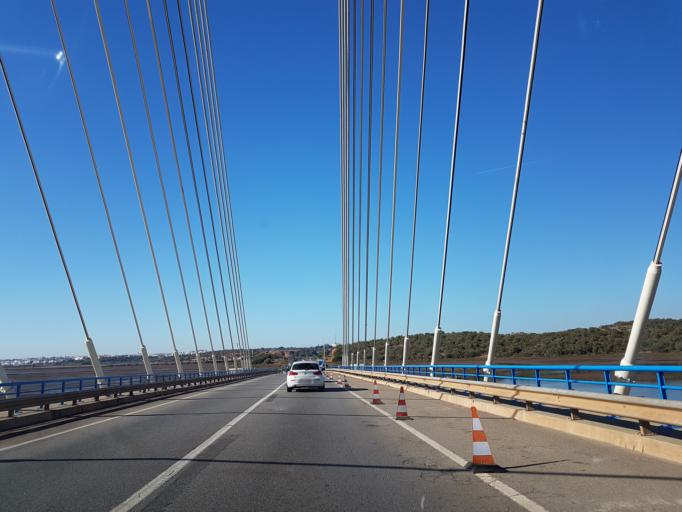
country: PT
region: Faro
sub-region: Lagoa
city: Estombar
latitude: 37.1515
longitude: -8.5081
